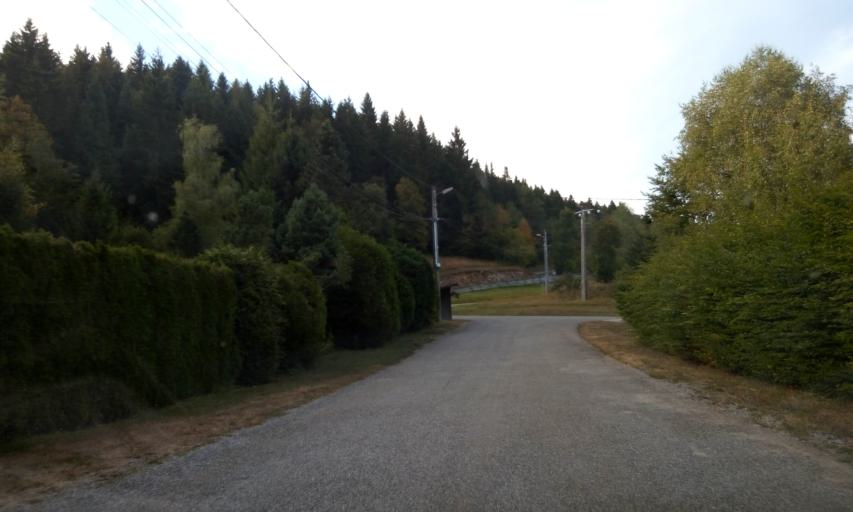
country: FR
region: Rhone-Alpes
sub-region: Departement de l'Ain
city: Martignat
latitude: 46.1874
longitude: 5.6751
